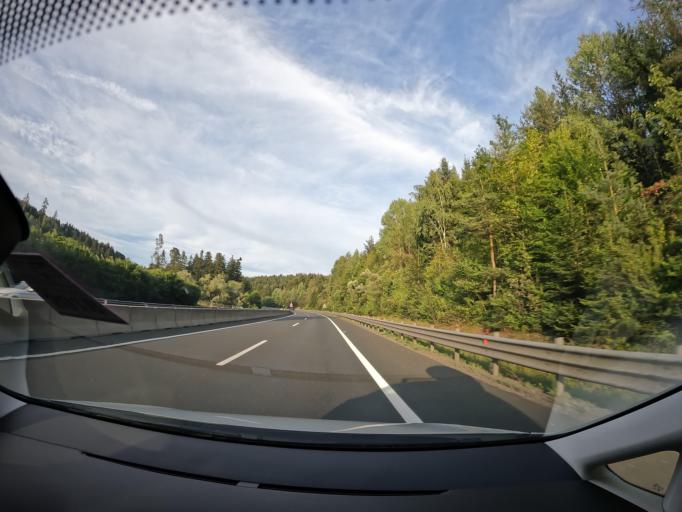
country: AT
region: Carinthia
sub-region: Politischer Bezirk Volkermarkt
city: Griffen
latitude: 46.7034
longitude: 14.7732
